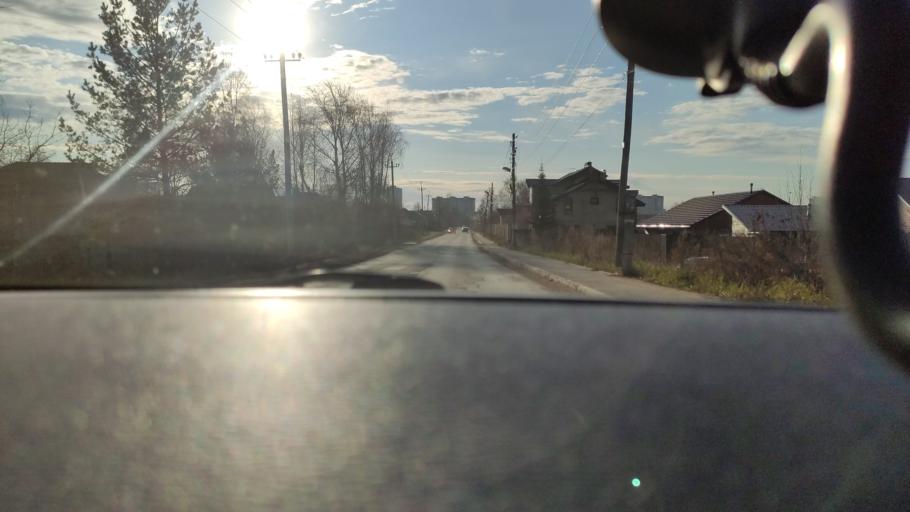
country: RU
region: Perm
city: Kondratovo
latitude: 58.0504
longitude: 56.0297
